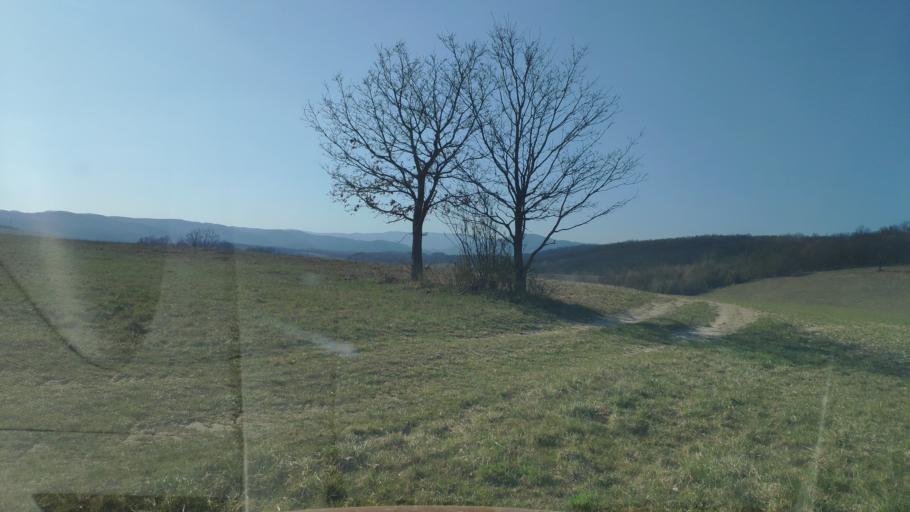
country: SK
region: Banskobystricky
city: Revuca
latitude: 48.5510
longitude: 20.2671
